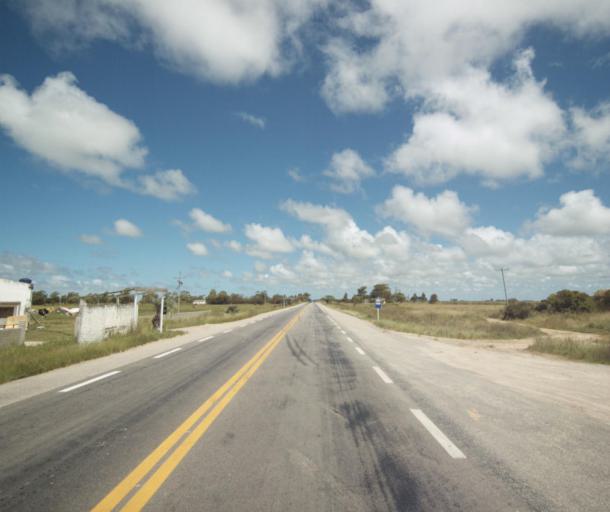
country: BR
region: Rio Grande do Sul
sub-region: Arroio Grande
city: Arroio Grande
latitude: -32.8540
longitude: -52.7040
